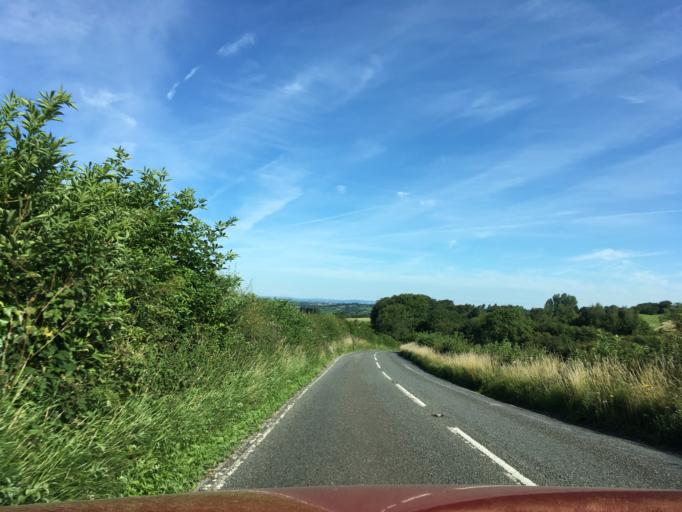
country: GB
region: England
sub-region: South Gloucestershire
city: Cold Ashton
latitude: 51.4363
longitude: -2.4086
